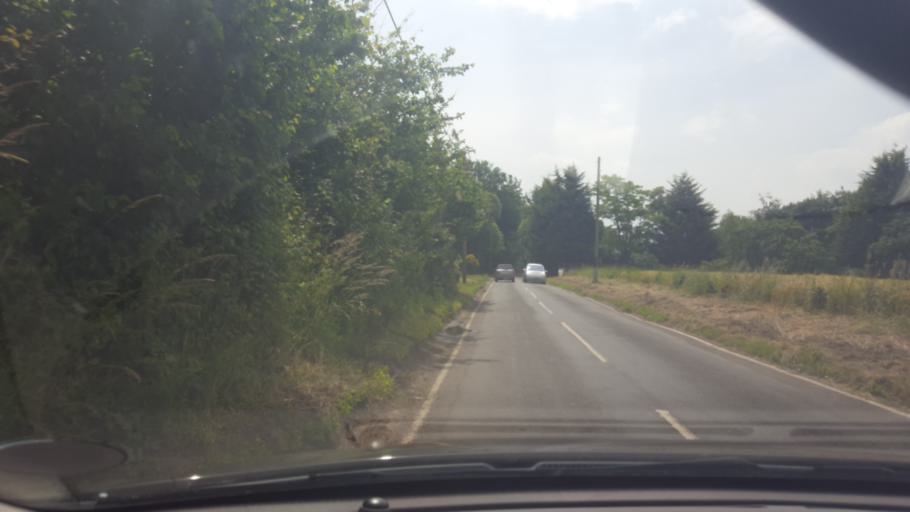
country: GB
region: England
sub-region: Essex
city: Little Clacton
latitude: 51.8715
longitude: 1.1242
